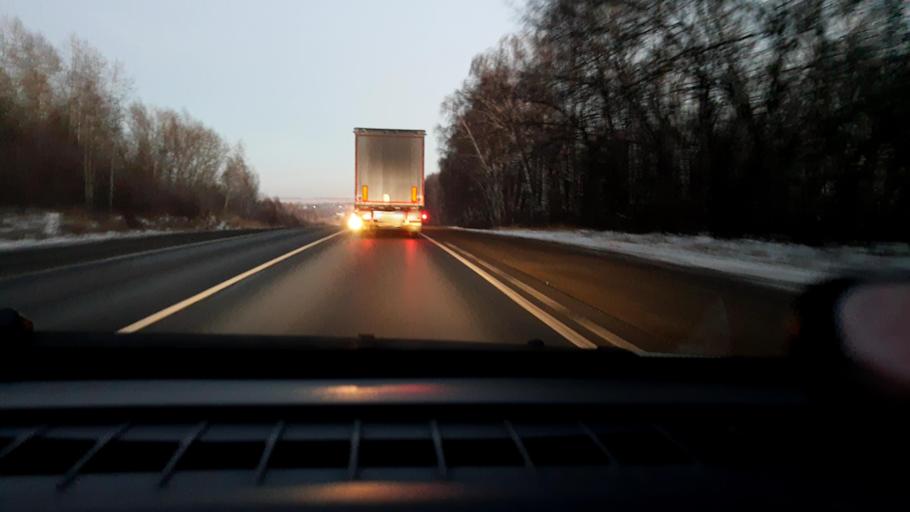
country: RU
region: Nizjnij Novgorod
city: Lyskovo
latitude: 56.0067
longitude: 44.8838
